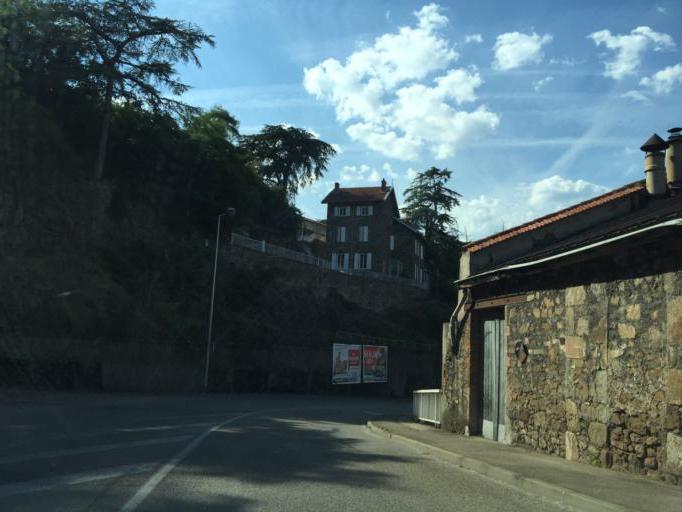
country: FR
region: Rhone-Alpes
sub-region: Departement de l'Ardeche
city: Annonay
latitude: 45.2352
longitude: 4.6719
